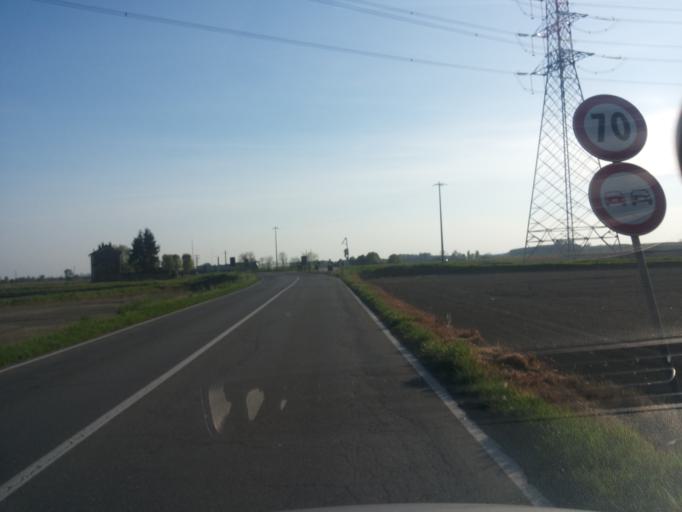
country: IT
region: Lombardy
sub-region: Provincia di Pavia
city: Castello d'Agogna
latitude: 45.2278
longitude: 8.6790
